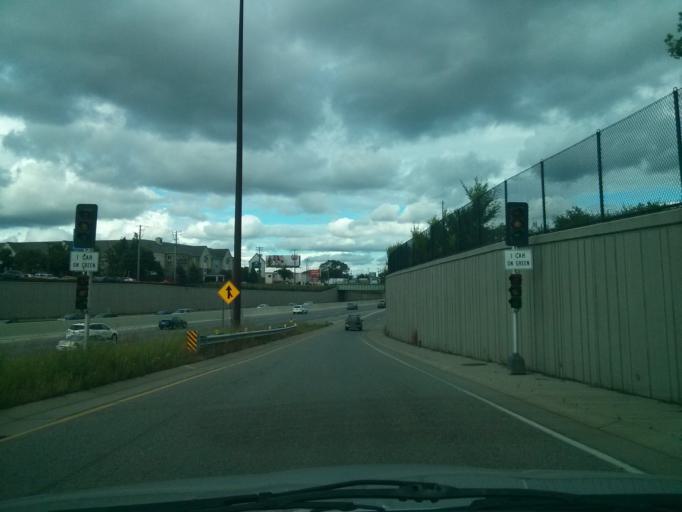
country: US
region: Minnesota
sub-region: Hennepin County
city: Richfield
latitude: 44.8615
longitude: -93.2863
